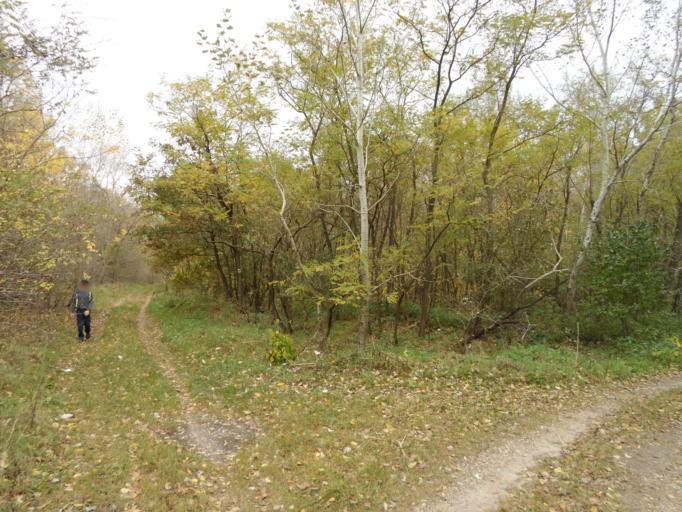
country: HU
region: Fejer
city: Szekesfehervar
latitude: 47.2232
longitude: 18.3567
